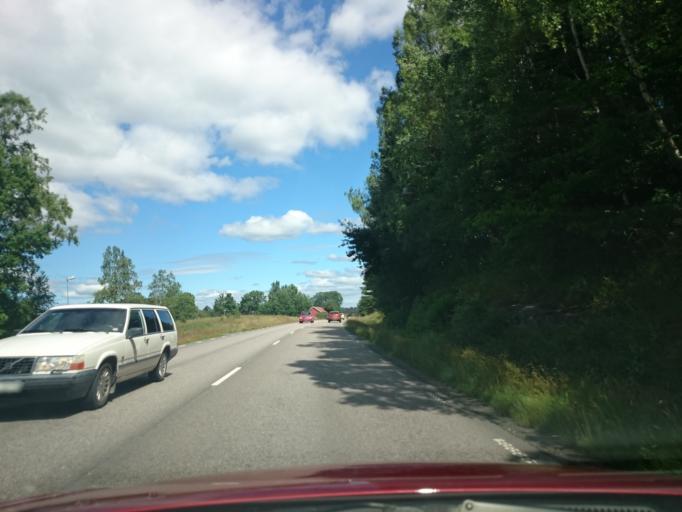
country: SE
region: Vaestra Goetaland
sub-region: Lerums Kommun
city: Stenkullen
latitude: 57.8109
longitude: 12.3017
